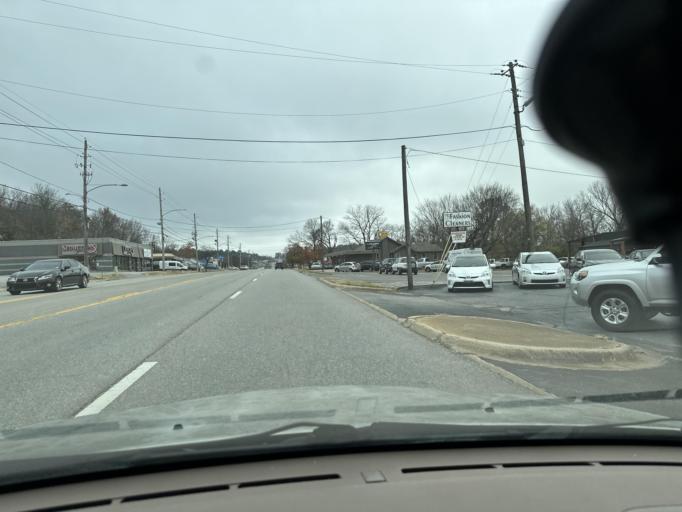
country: US
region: Arkansas
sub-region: Washington County
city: Fayetteville
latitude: 36.0934
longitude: -94.1532
